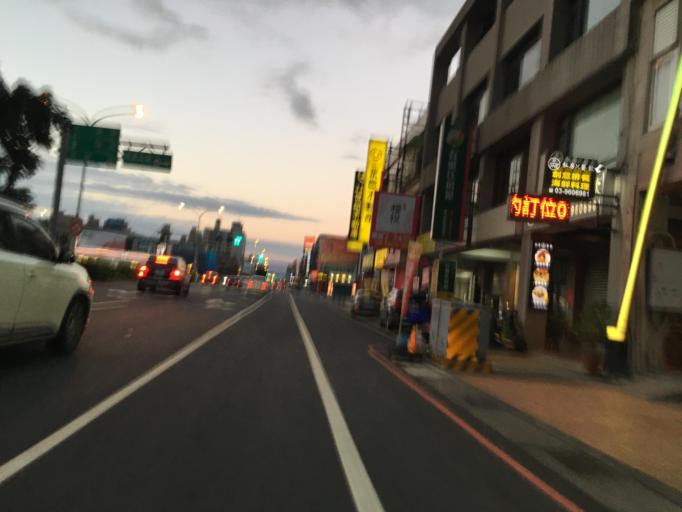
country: TW
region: Taiwan
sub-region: Yilan
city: Yilan
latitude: 24.6770
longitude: 121.7778
